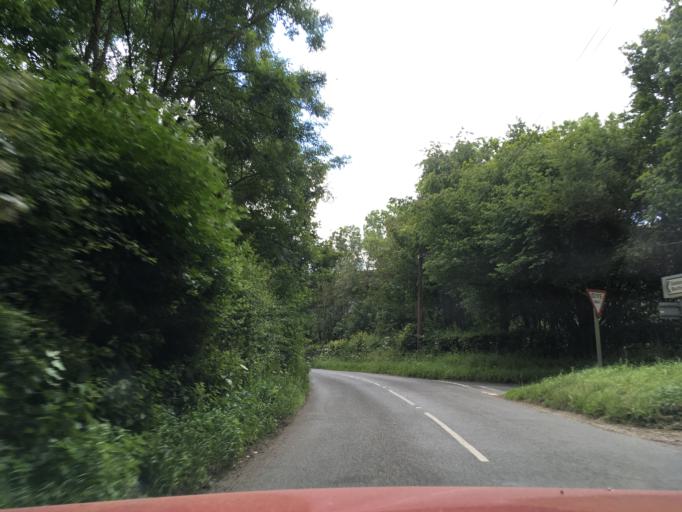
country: GB
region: England
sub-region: West Berkshire
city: Welford
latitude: 51.4513
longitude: -1.4069
